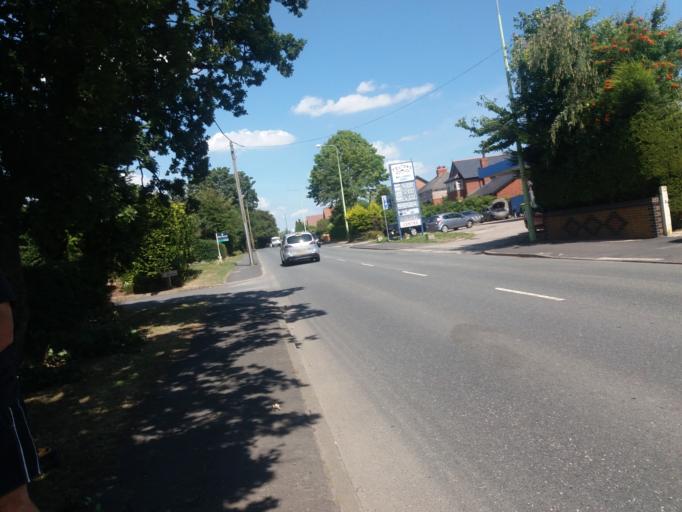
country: GB
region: England
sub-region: Lancashire
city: Euxton
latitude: 53.6735
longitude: -2.6773
